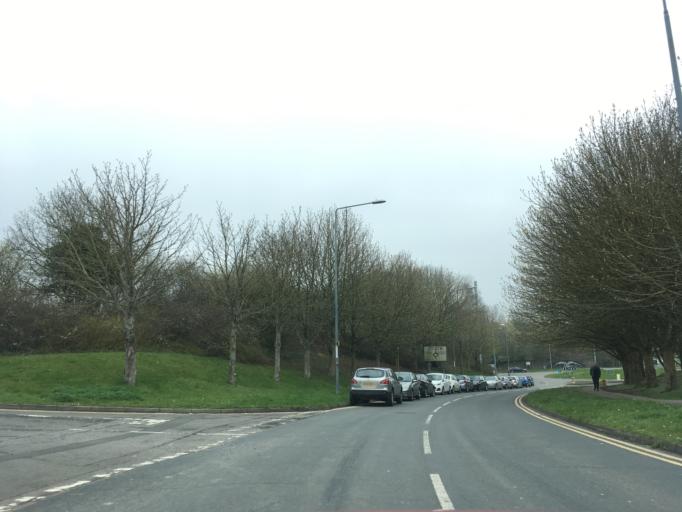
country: GB
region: Wales
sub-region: Newport
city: Newport
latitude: 51.5575
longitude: -3.0311
